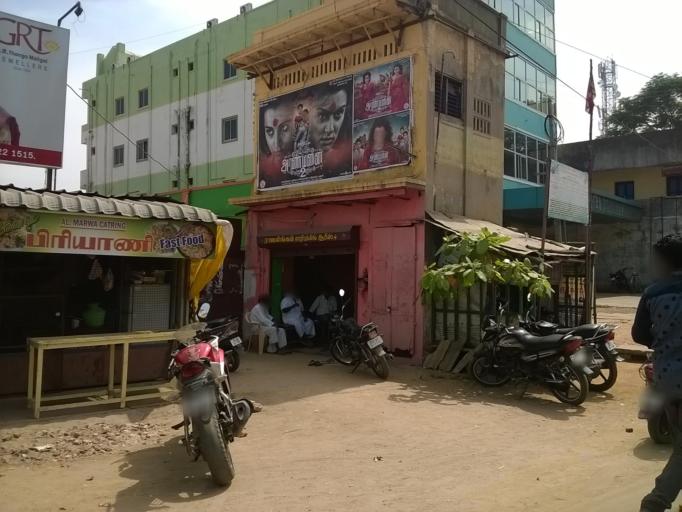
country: IN
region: Tamil Nadu
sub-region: Cuddalore
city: Panruti
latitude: 11.7708
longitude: 79.5509
